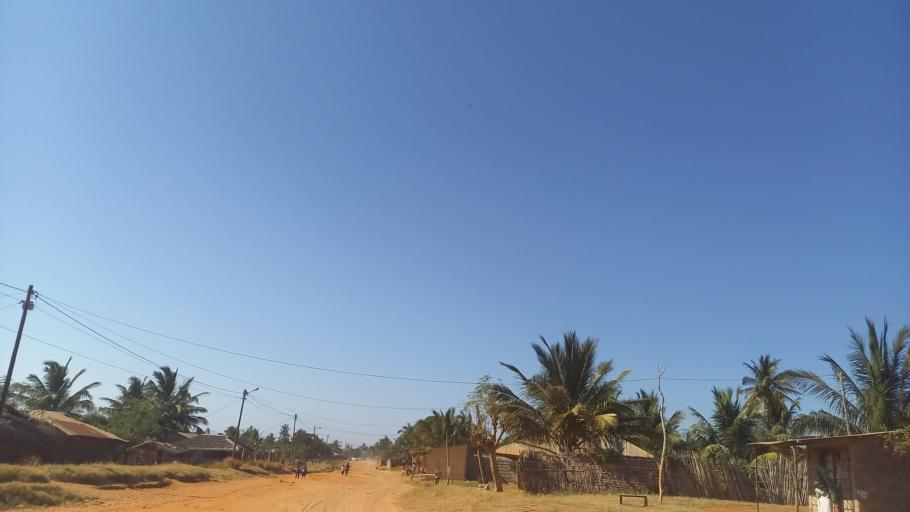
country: MZ
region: Cabo Delgado
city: Pemba
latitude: -13.1373
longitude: 40.5502
